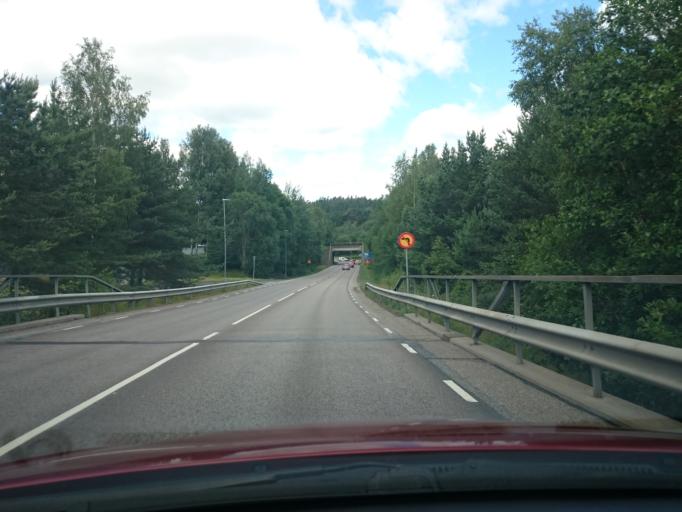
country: SE
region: Vaestra Goetaland
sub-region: Lerums Kommun
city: Lerum
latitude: 57.7759
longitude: 12.2877
